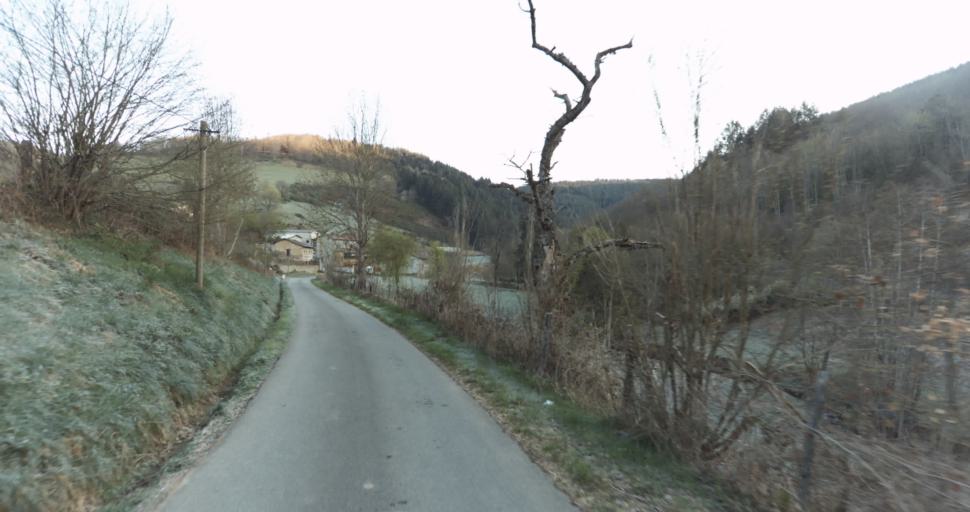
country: FR
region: Rhone-Alpes
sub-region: Departement du Rhone
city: Tarare
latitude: 45.8975
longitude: 4.3997
